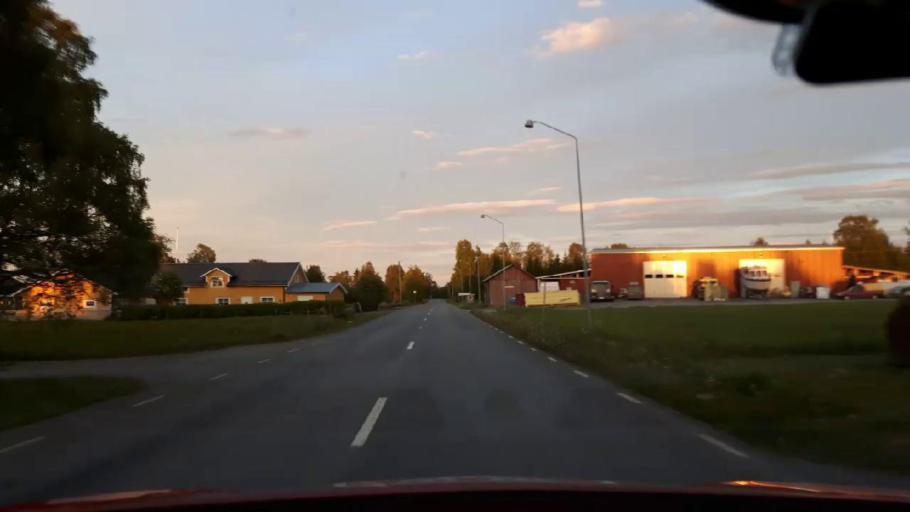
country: SE
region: Jaemtland
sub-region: OEstersunds Kommun
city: Ostersund
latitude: 63.1174
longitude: 14.7215
